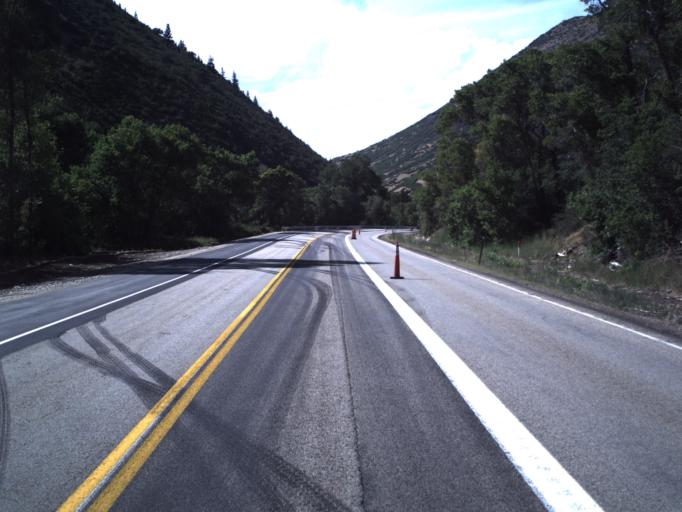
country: US
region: Utah
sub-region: Wasatch County
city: Heber
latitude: 40.4014
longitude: -111.3066
